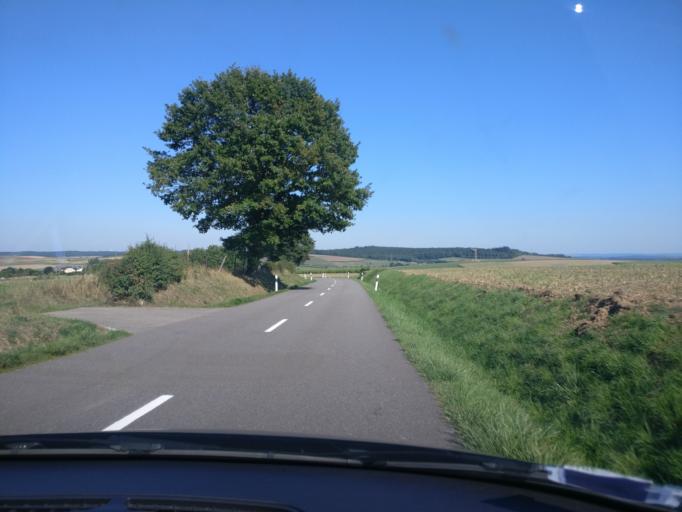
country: LU
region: Grevenmacher
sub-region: Canton d'Echternach
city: Bech
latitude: 49.7238
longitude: 6.3318
